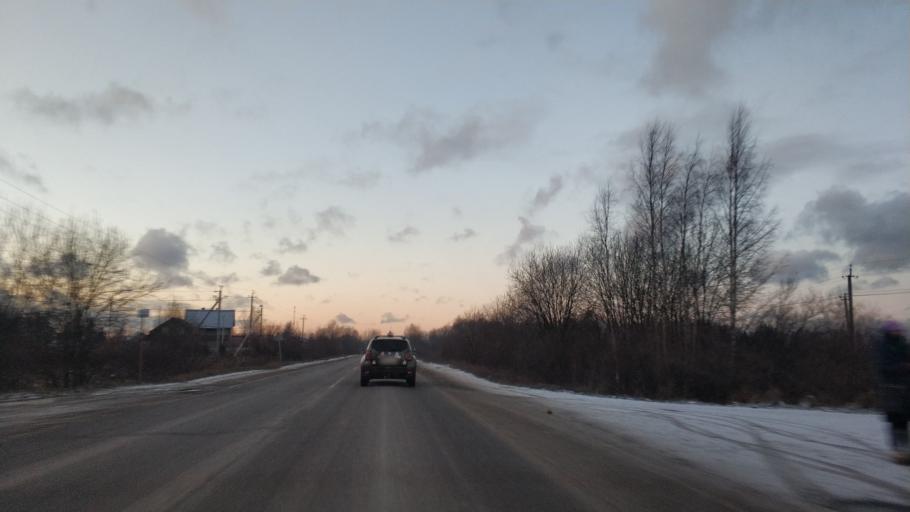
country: RU
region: St.-Petersburg
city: Pontonnyy
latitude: 59.8041
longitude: 30.6277
